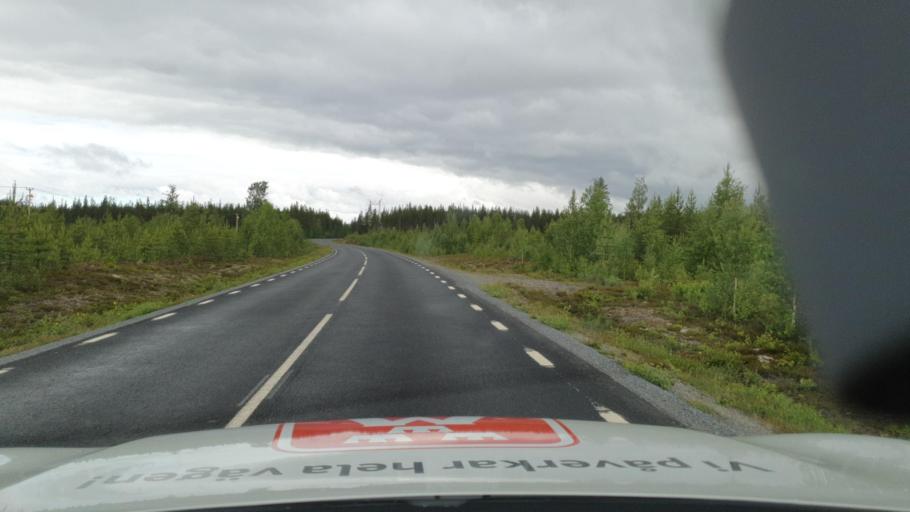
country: SE
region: Vaesterbotten
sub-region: Dorotea Kommun
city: Dorotea
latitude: 64.1977
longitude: 16.5765
